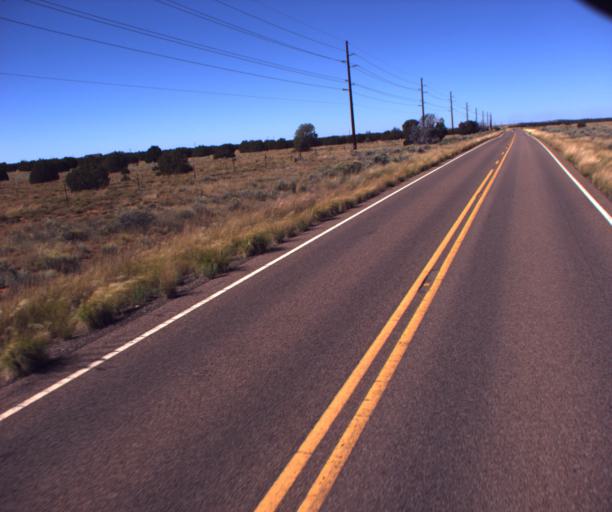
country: US
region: Arizona
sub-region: Navajo County
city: Taylor
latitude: 34.4831
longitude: -110.2812
